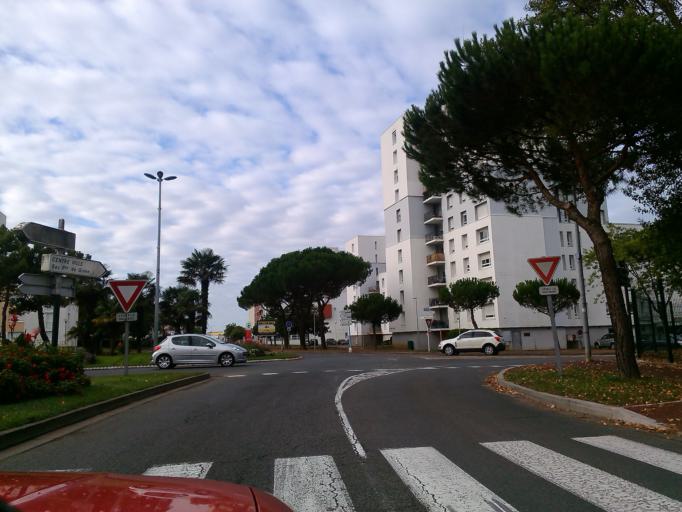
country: FR
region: Poitou-Charentes
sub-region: Departement de la Charente-Maritime
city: Royan
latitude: 45.6368
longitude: -1.0286
